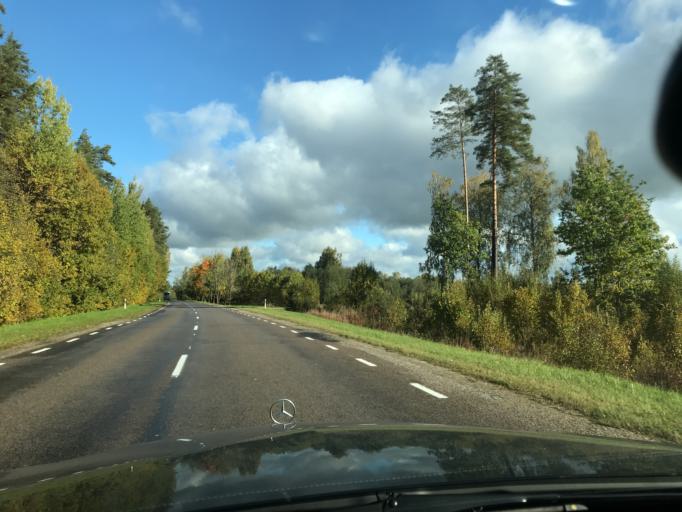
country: EE
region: Valgamaa
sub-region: Torva linn
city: Torva
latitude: 57.9977
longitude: 26.0783
